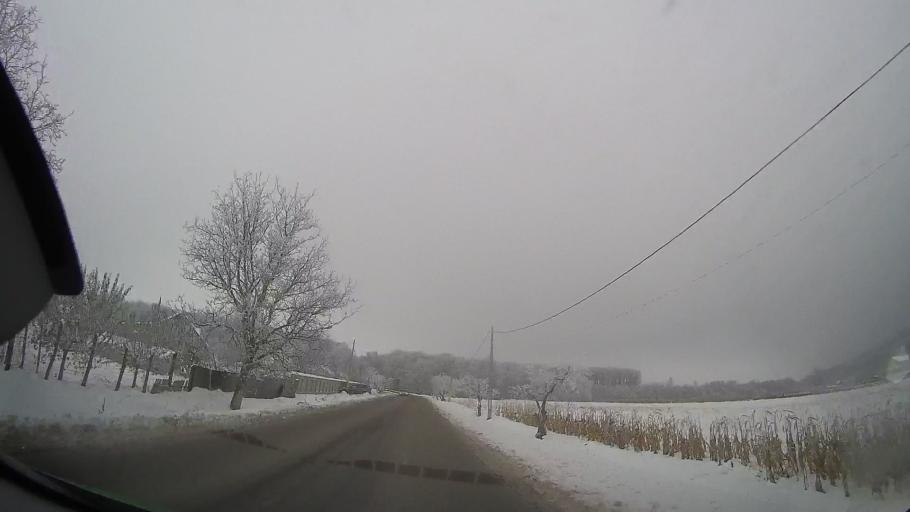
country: RO
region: Neamt
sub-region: Comuna Horia
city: Cotu Vames
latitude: 46.8791
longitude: 26.9743
